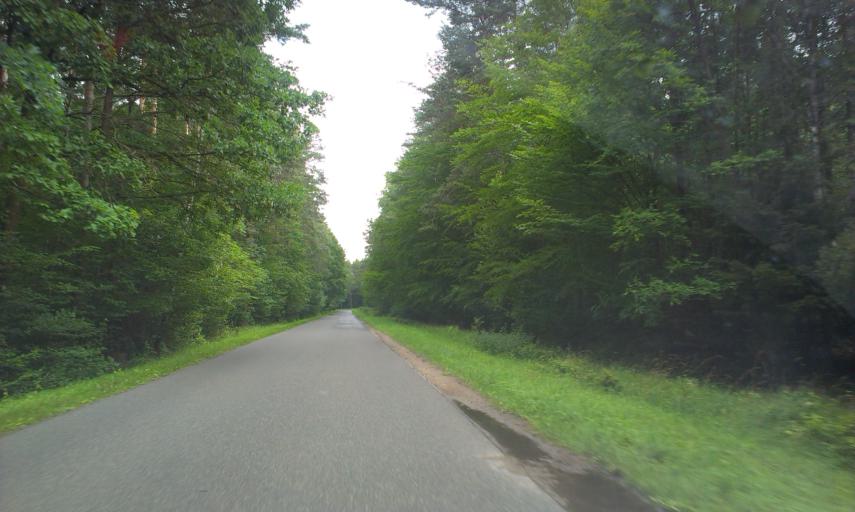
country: PL
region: Greater Poland Voivodeship
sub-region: Powiat zlotowski
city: Okonek
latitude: 53.5333
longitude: 16.9223
